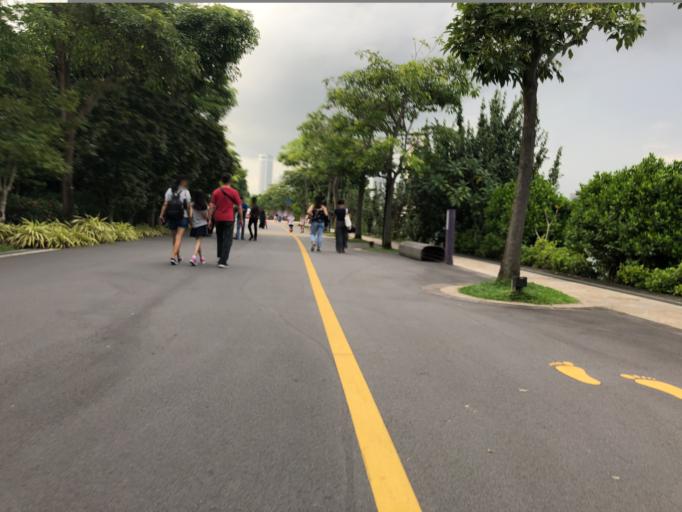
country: SG
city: Singapore
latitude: 1.2828
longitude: 103.8687
